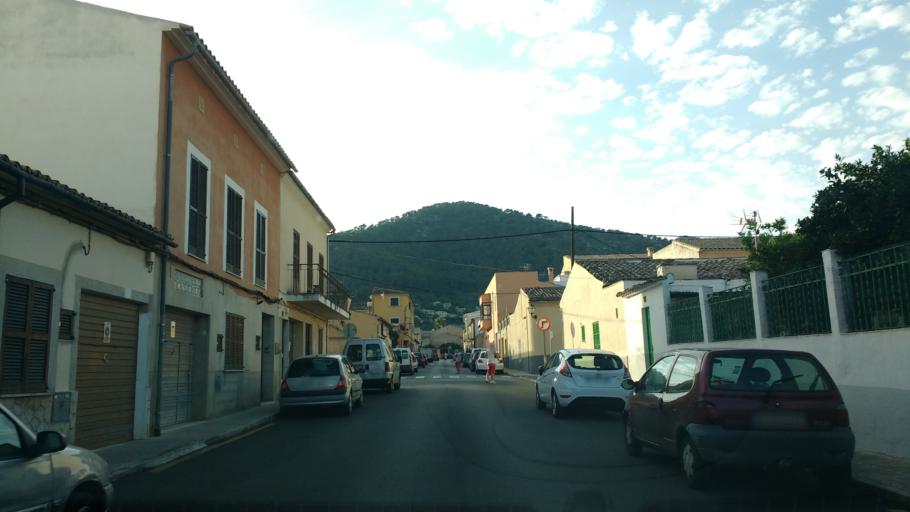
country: ES
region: Balearic Islands
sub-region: Illes Balears
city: Alaro
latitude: 39.7050
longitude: 2.7946
